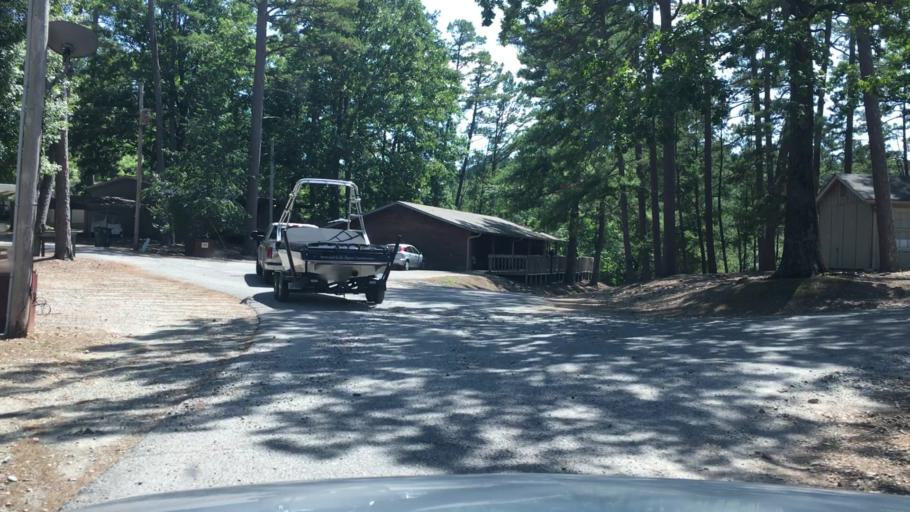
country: US
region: Arkansas
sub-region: Garland County
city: Piney
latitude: 34.5464
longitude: -93.3619
